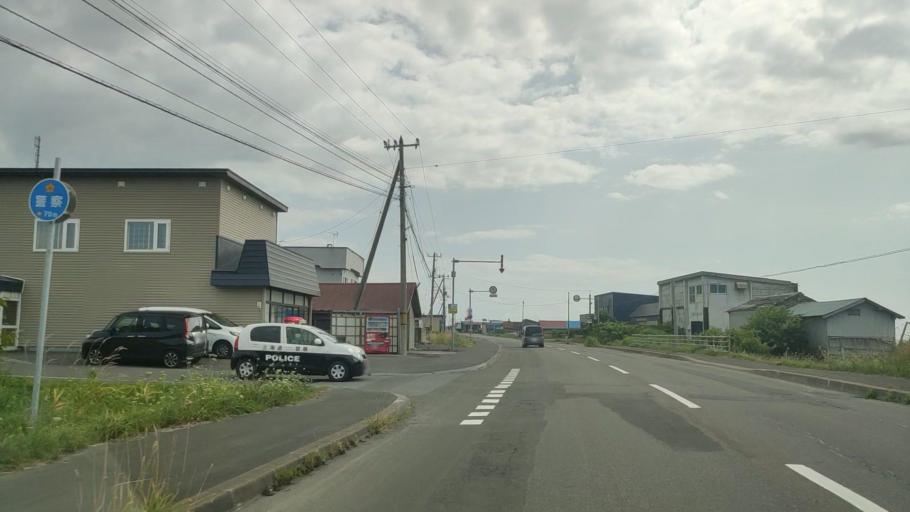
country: JP
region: Hokkaido
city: Rumoi
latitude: 44.1503
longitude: 141.6543
